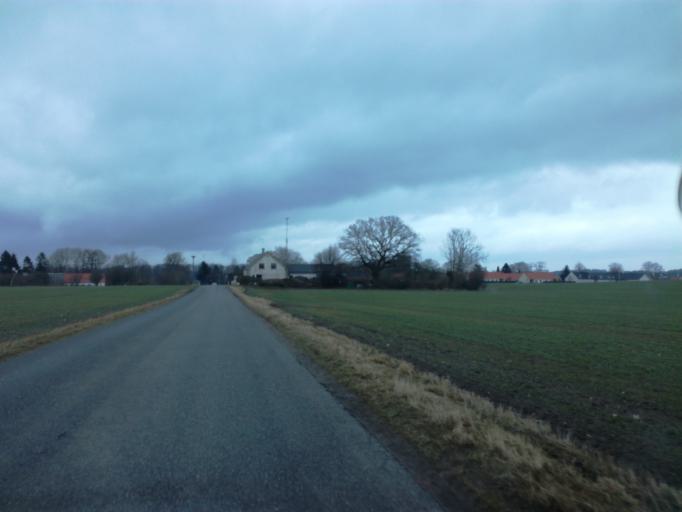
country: DK
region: South Denmark
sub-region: Vejle Kommune
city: Borkop
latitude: 55.6034
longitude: 9.6404
